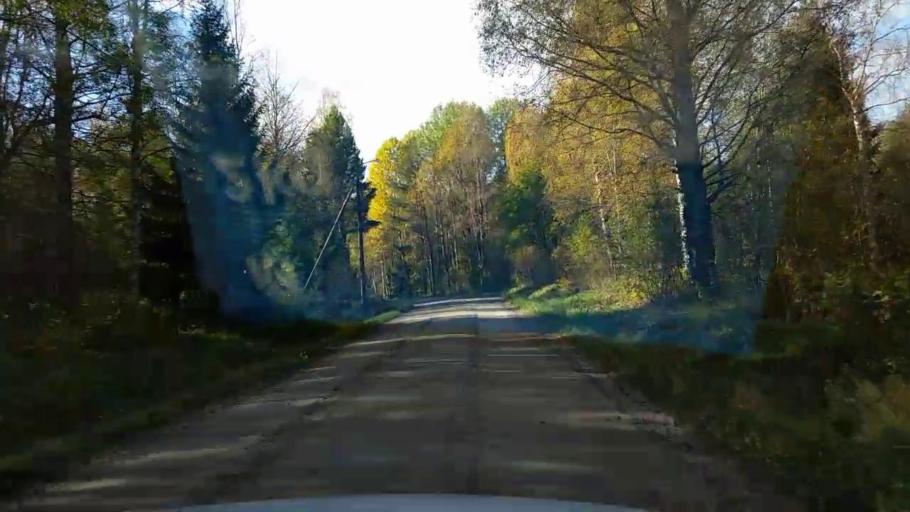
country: SE
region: Gaevleborg
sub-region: Ljusdals Kommun
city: Jaervsoe
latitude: 61.7924
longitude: 16.2022
